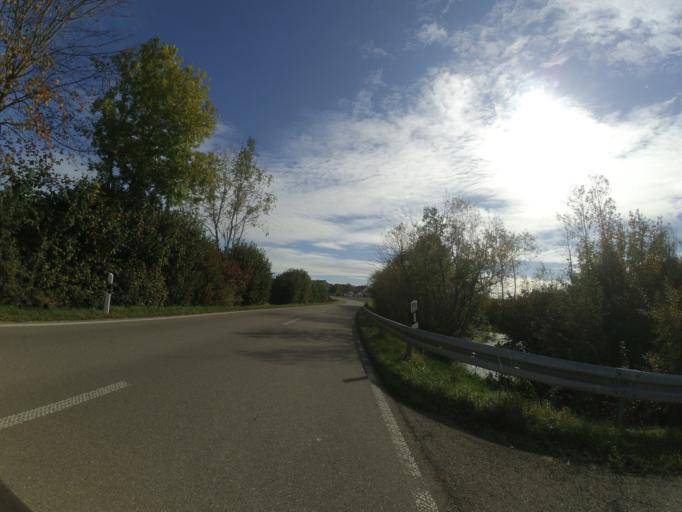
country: DE
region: Baden-Wuerttemberg
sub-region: Tuebingen Region
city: Lonsee
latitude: 48.6052
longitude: 9.9363
